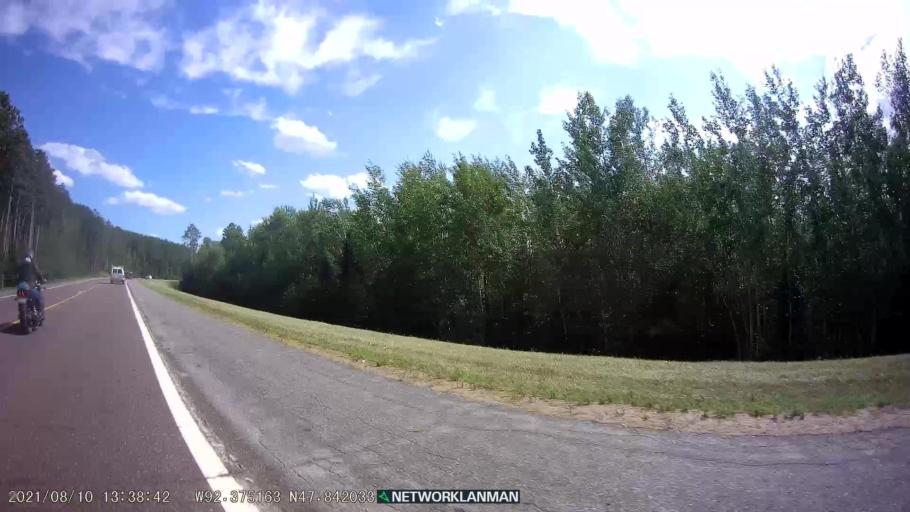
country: US
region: Minnesota
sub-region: Saint Louis County
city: Aurora
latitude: 47.8423
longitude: -92.3748
